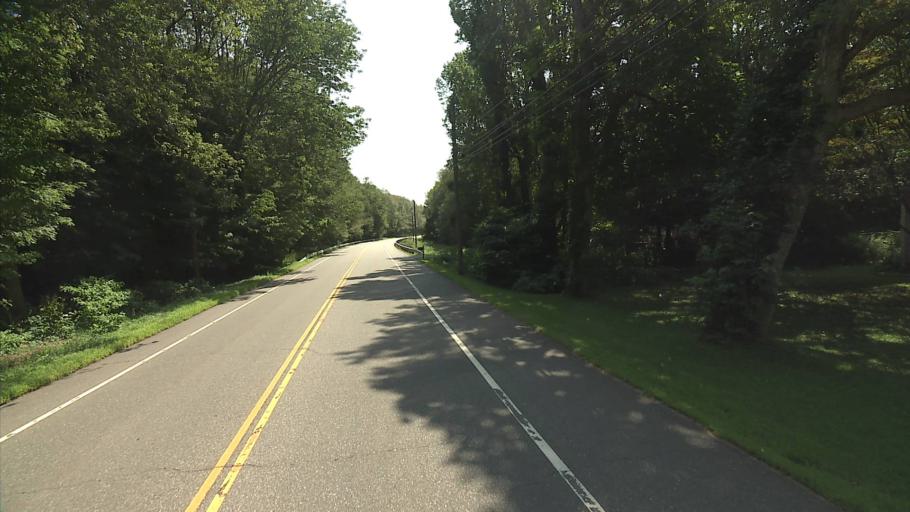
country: US
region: Connecticut
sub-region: New London County
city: Colchester
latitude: 41.5606
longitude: -72.3071
